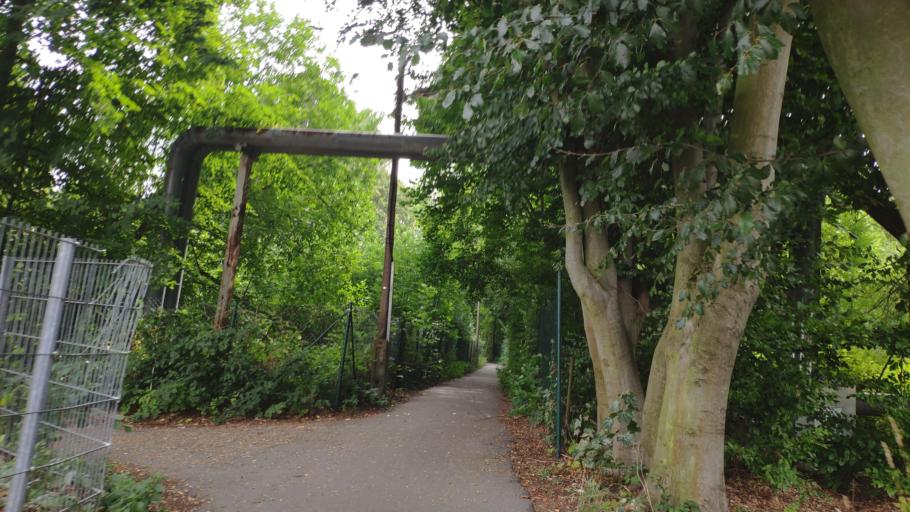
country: DE
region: Saxony
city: Chemnitz
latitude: 50.8117
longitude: 12.9480
